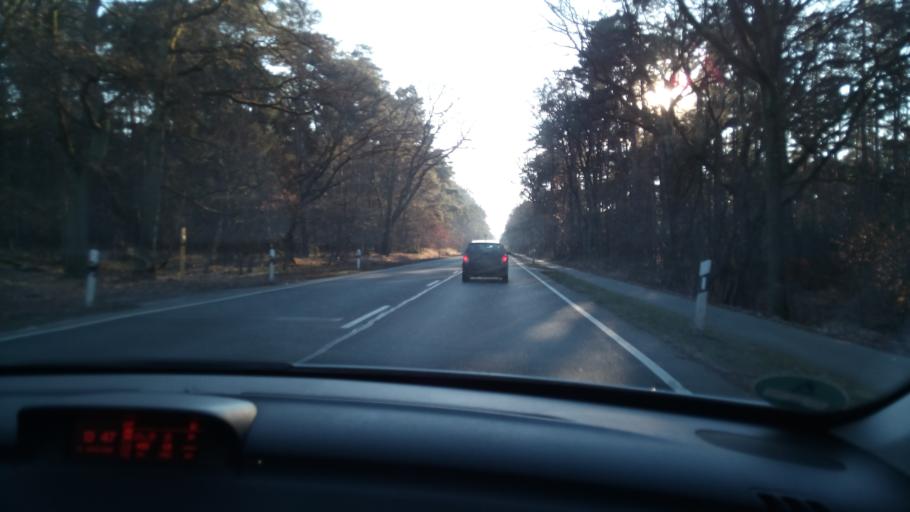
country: DE
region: Lower Saxony
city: Adendorf
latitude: 53.3067
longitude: 10.4293
